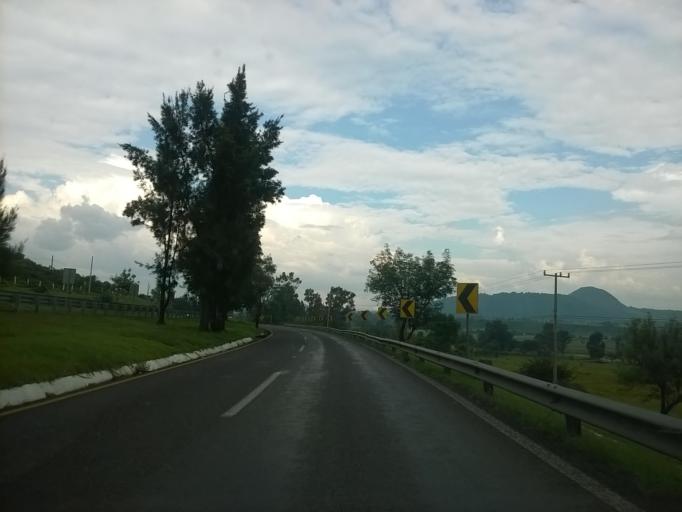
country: MX
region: Michoacan
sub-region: Huiramba
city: El Pedregal
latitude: 19.5303
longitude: -101.4799
